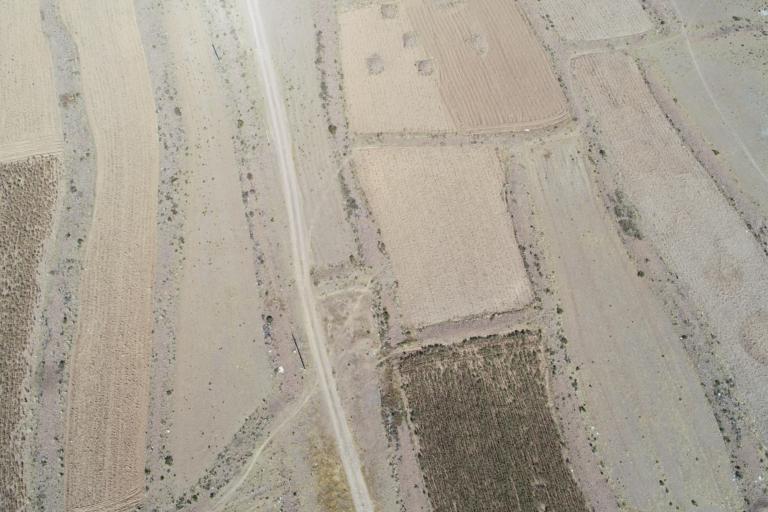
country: BO
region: La Paz
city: Achacachi
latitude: -15.9011
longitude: -68.9072
